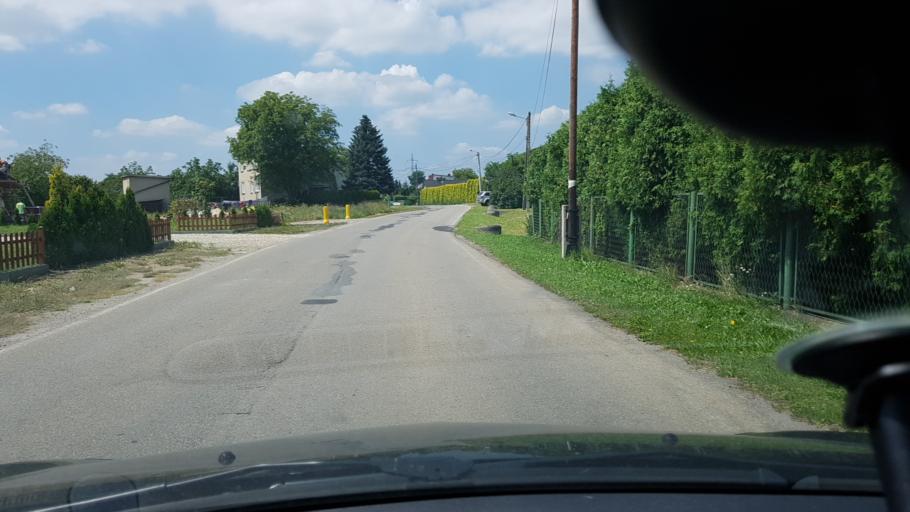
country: PL
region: Lesser Poland Voivodeship
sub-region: Powiat oswiecimski
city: Babice
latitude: 50.0552
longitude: 19.1983
